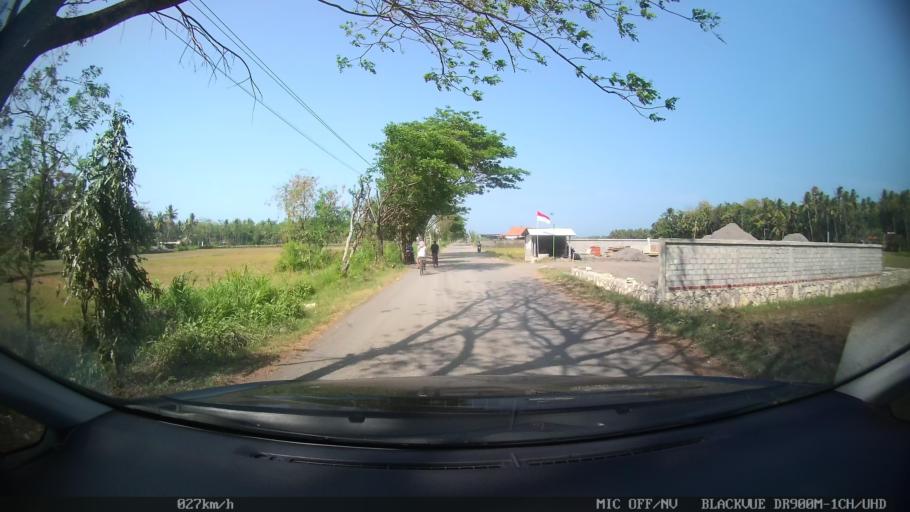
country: ID
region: Daerah Istimewa Yogyakarta
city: Srandakan
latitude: -7.9589
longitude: 110.2160
